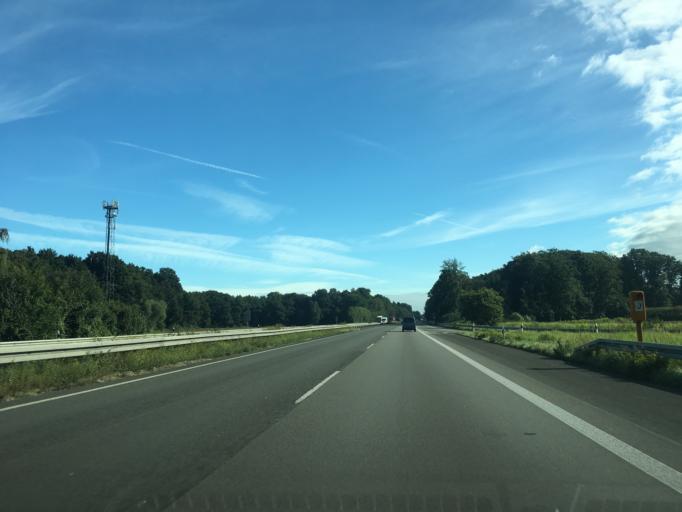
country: DE
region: North Rhine-Westphalia
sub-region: Regierungsbezirk Munster
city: Greven
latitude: 52.0850
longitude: 7.6456
